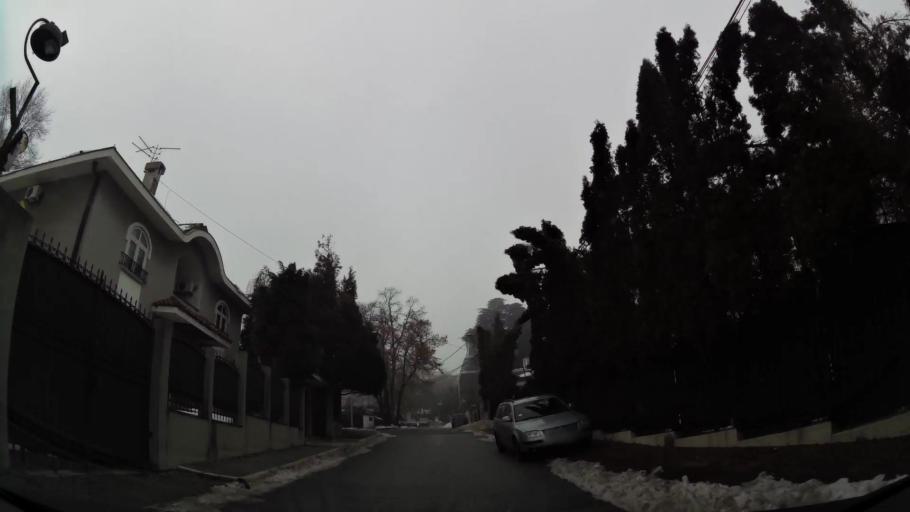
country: RS
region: Central Serbia
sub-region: Belgrade
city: Savski Venac
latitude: 44.7790
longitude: 20.4625
